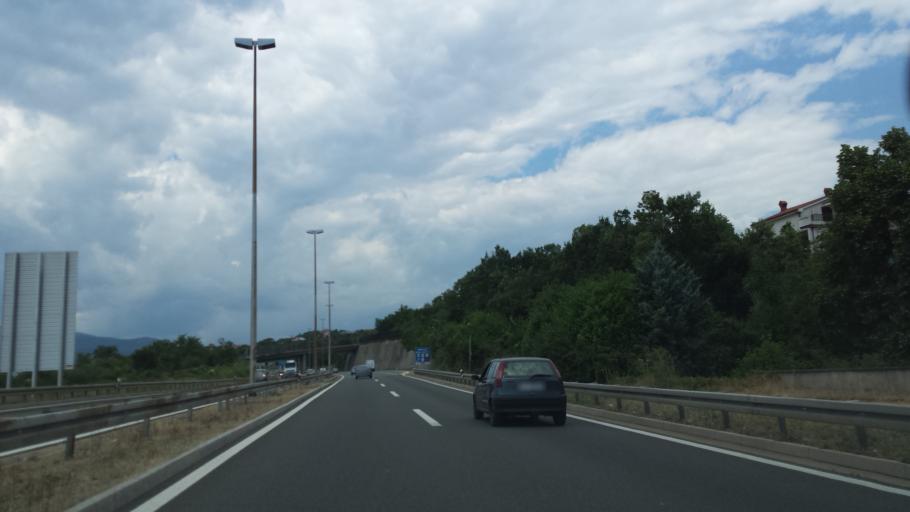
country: HR
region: Primorsko-Goranska
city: Rubesi
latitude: 45.3523
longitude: 14.3591
